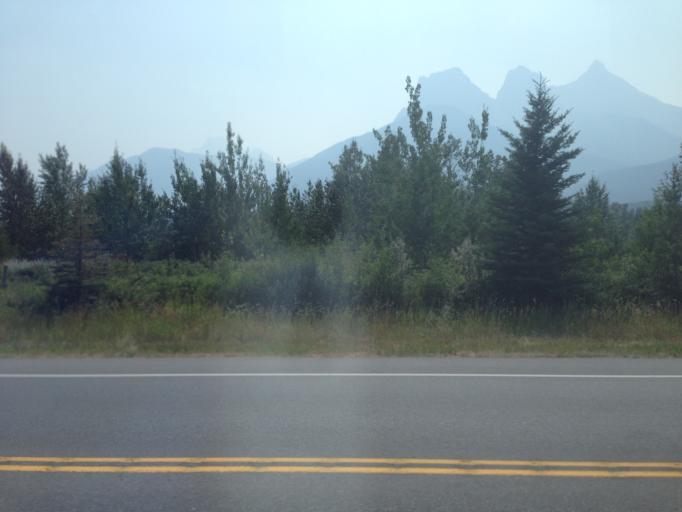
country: CA
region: Alberta
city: Canmore
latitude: 51.0750
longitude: -115.3291
